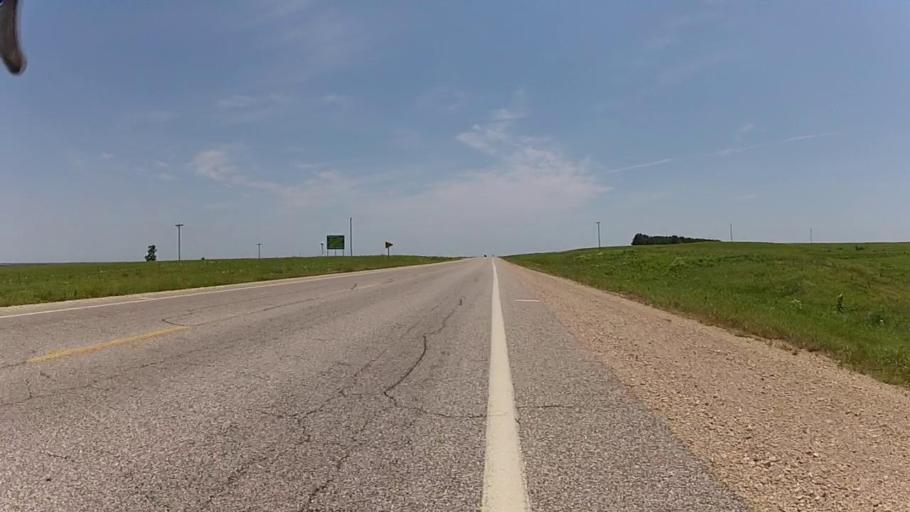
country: US
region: Kansas
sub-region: Chautauqua County
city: Sedan
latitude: 37.1114
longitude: -96.2571
